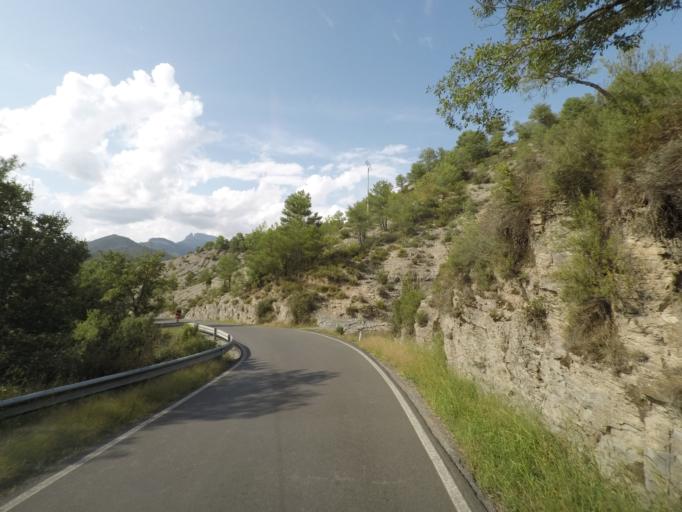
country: ES
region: Aragon
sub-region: Provincia de Huesca
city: Laspuna
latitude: 42.5082
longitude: 0.1304
